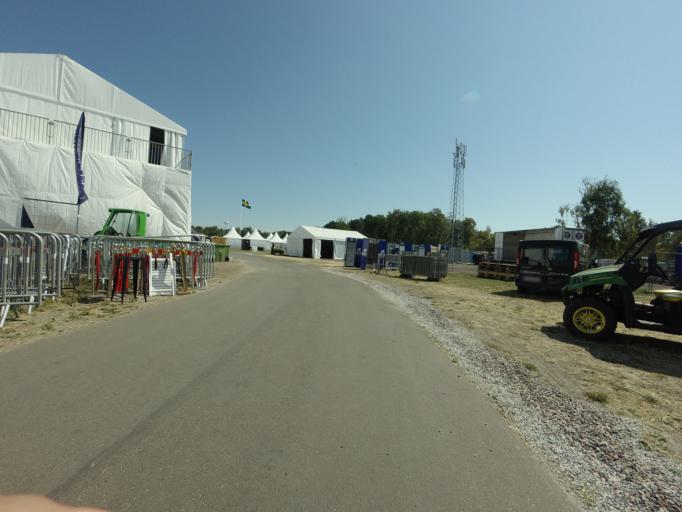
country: SE
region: Skane
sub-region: Vellinge Kommun
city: Skanor med Falsterbo
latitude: 55.3986
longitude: 12.8557
